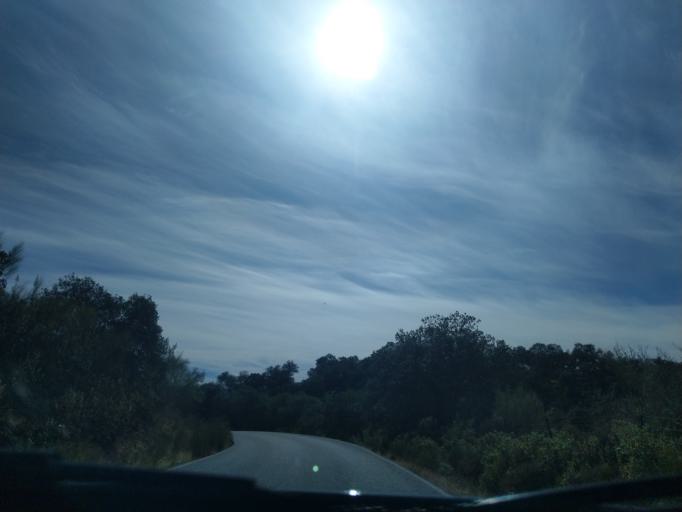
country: ES
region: Extremadura
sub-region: Provincia de Badajoz
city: Reina
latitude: 38.1387
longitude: -5.9165
